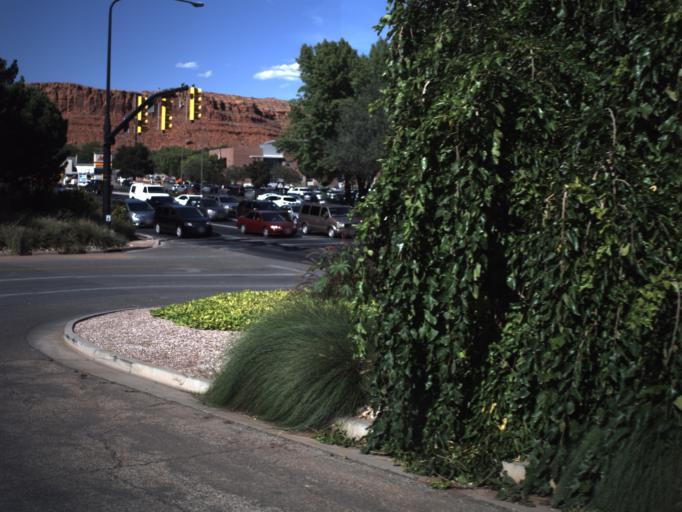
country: US
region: Utah
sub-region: Washington County
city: Saint George
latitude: 37.1096
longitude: -113.5941
